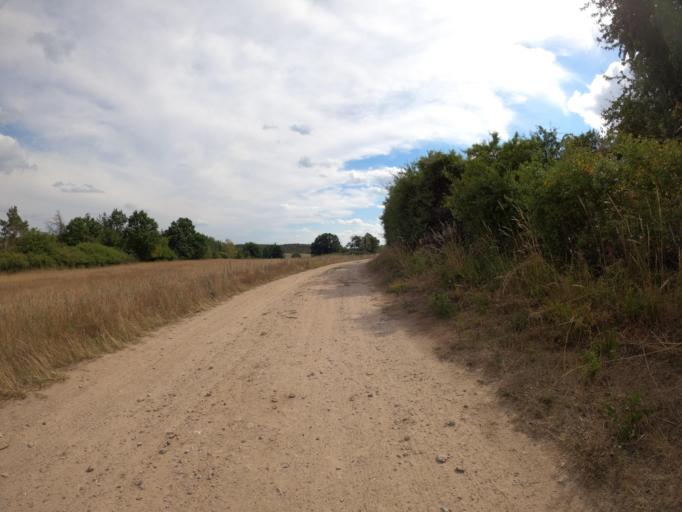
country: DE
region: Mecklenburg-Vorpommern
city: Loitz
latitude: 53.3202
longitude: 13.4286
